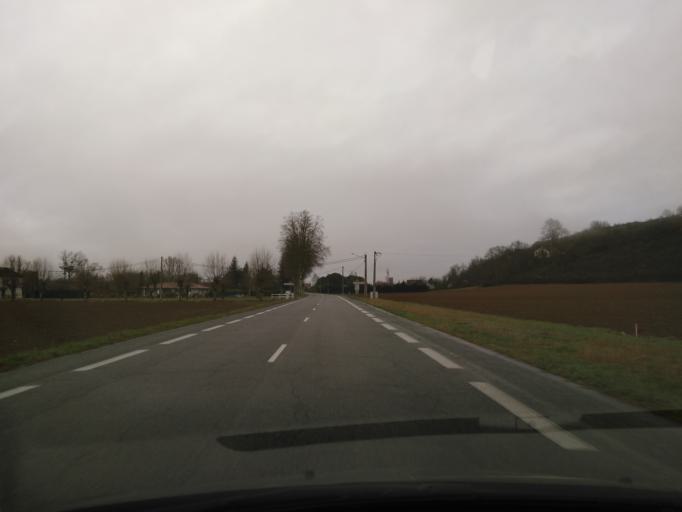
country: FR
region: Midi-Pyrenees
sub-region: Departement de la Haute-Garonne
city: Rieux-Volvestre
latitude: 43.2479
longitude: 1.2022
